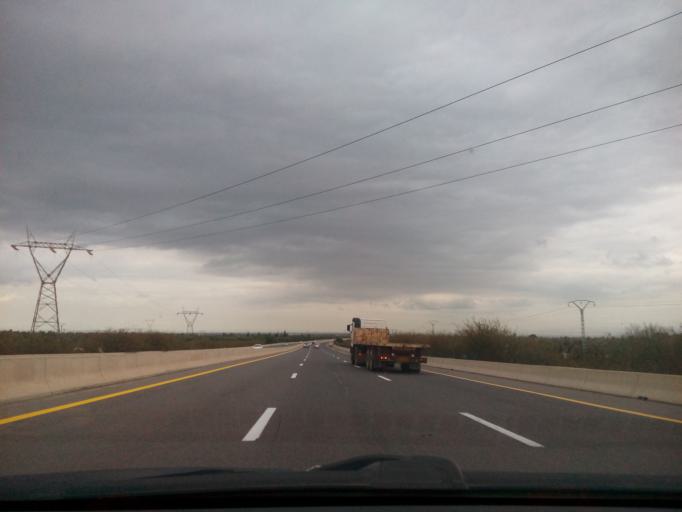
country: DZ
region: Mascara
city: Sig
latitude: 35.5776
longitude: -0.2585
